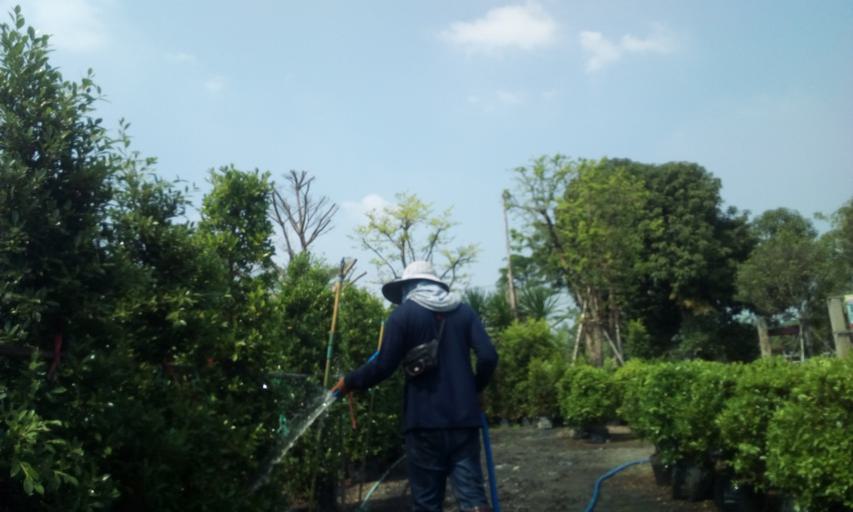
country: TH
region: Nakhon Nayok
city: Ongkharak
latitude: 14.1295
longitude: 100.9498
